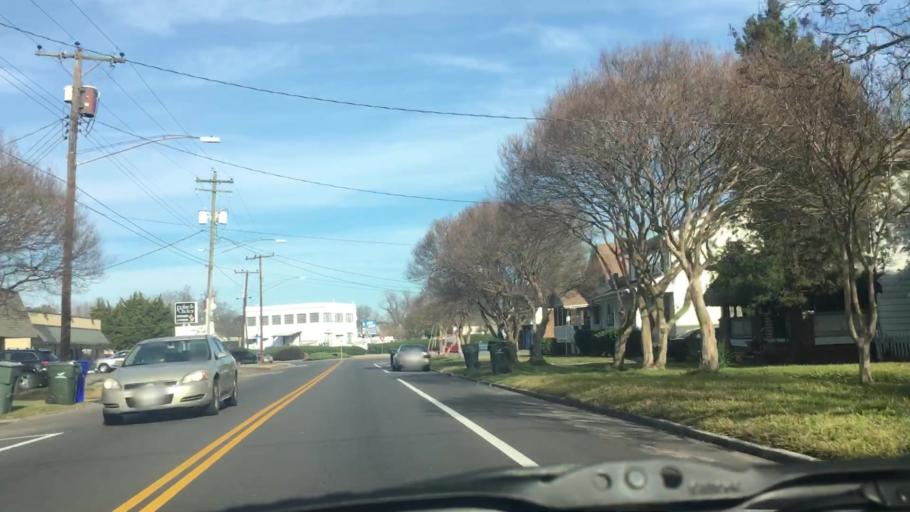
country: US
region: Virginia
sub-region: City of Norfolk
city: Norfolk
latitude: 36.8737
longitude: -76.2531
